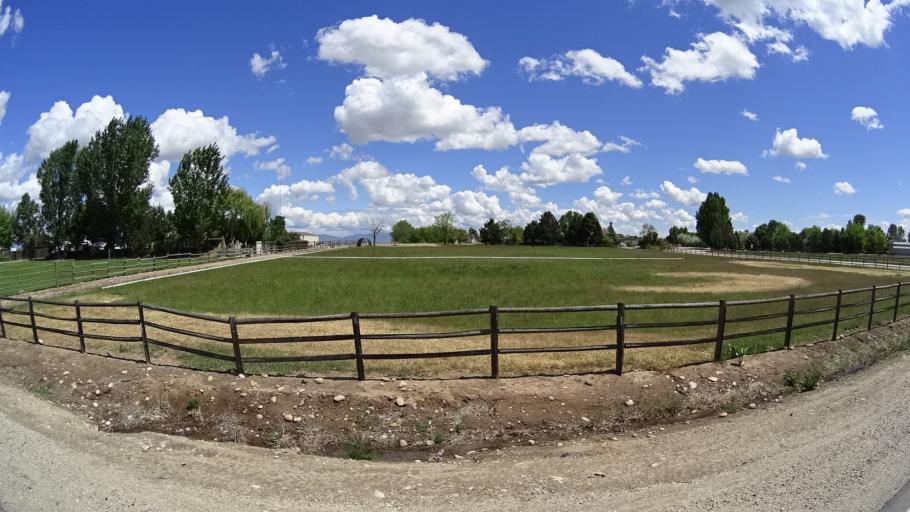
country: US
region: Idaho
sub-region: Ada County
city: Meridian
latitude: 43.5827
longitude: -116.4338
